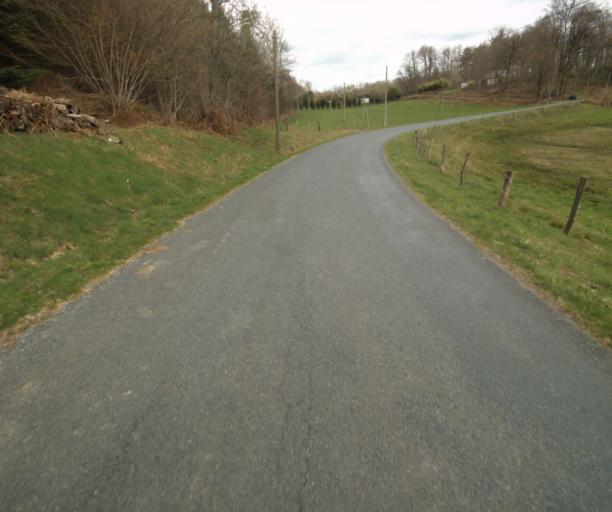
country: FR
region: Limousin
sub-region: Departement de la Correze
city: Correze
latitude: 45.3633
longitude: 1.9273
